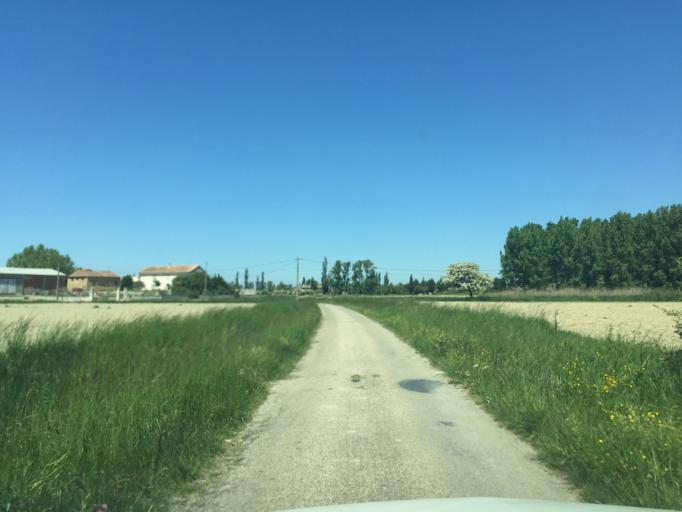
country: FR
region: Provence-Alpes-Cote d'Azur
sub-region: Departement du Vaucluse
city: Caderousse
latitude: 44.0979
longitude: 4.7855
